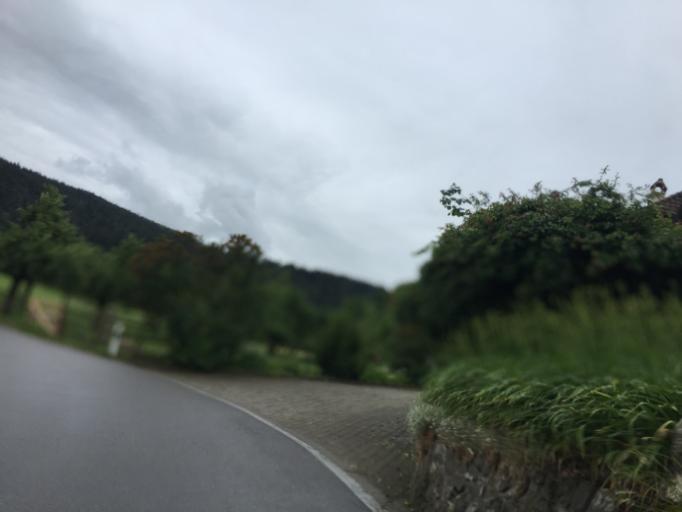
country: CH
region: Bern
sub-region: Bern-Mittelland District
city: Biglen
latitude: 46.9091
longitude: 7.6086
